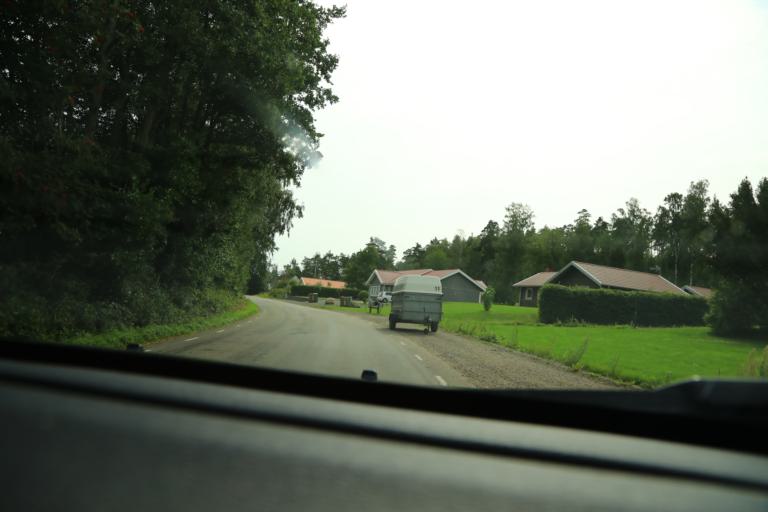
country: SE
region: Halland
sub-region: Varbergs Kommun
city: Varberg
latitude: 57.1786
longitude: 12.2219
